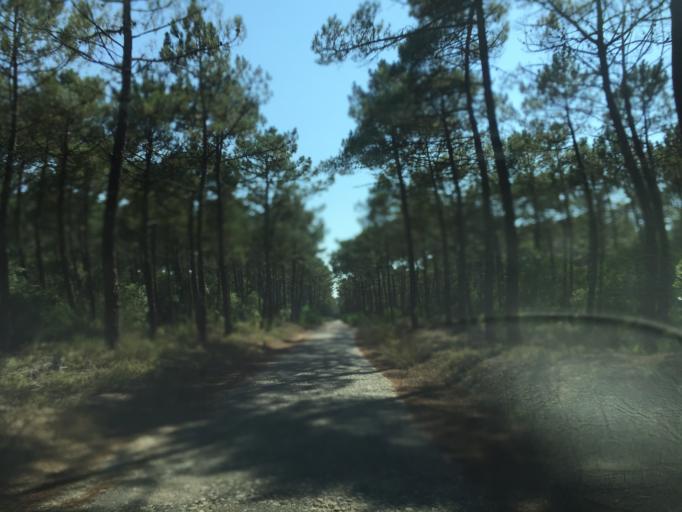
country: PT
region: Coimbra
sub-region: Figueira da Foz
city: Tavarede
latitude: 40.2459
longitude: -8.8448
